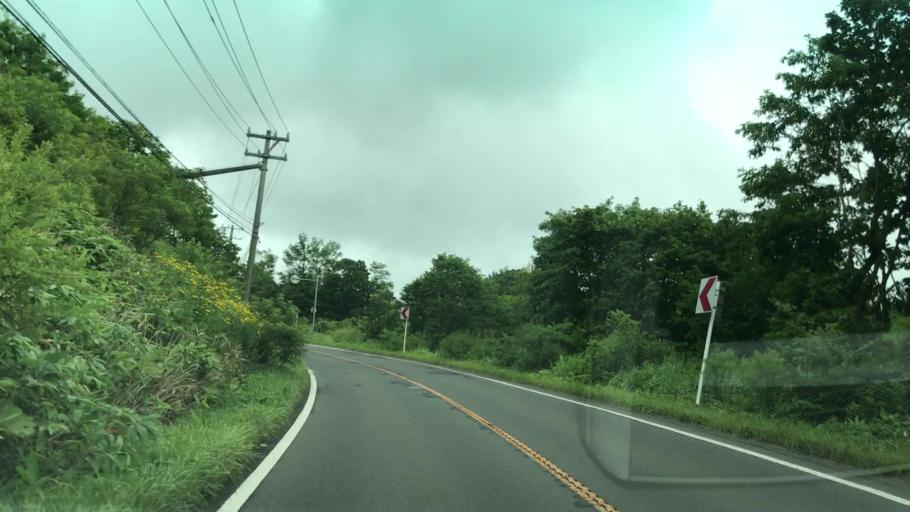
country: JP
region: Hokkaido
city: Muroran
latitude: 42.3794
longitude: 140.9721
